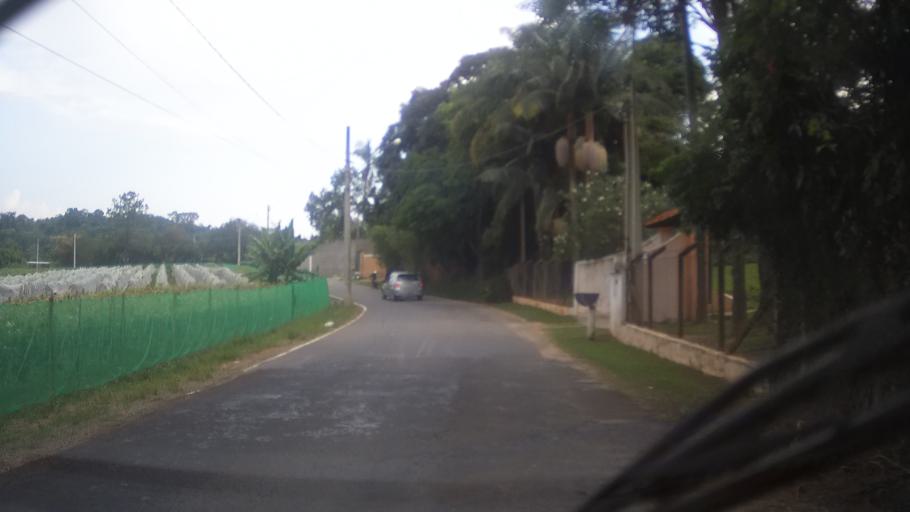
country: BR
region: Sao Paulo
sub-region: Itupeva
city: Itupeva
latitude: -23.1866
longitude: -47.1043
